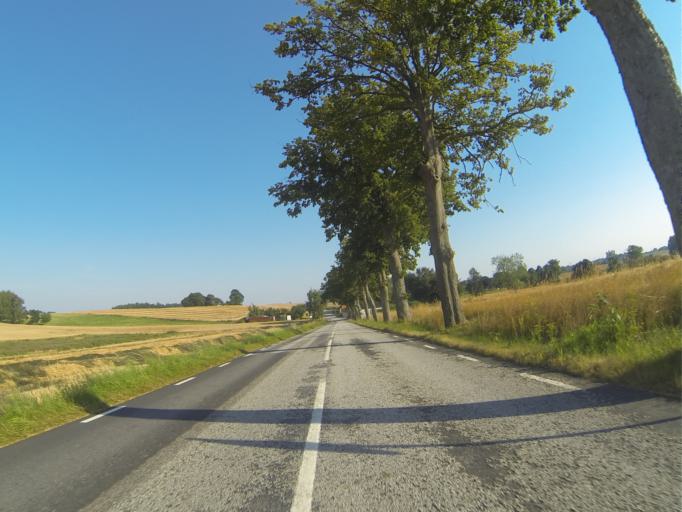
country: SE
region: Skane
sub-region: Svedala Kommun
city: Klagerup
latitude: 55.5873
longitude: 13.2784
